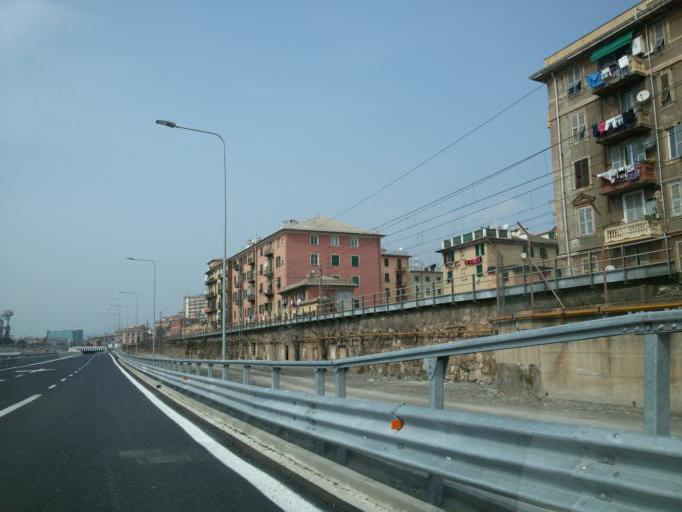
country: IT
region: Liguria
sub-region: Provincia di Genova
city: San Teodoro
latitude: 44.4136
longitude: 8.8699
